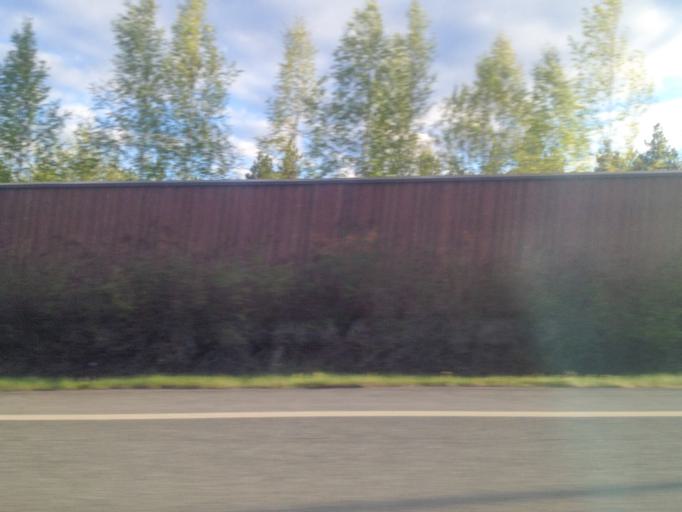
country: FI
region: Pirkanmaa
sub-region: Etelae-Pirkanmaa
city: Akaa
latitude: 61.1845
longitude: 23.8834
